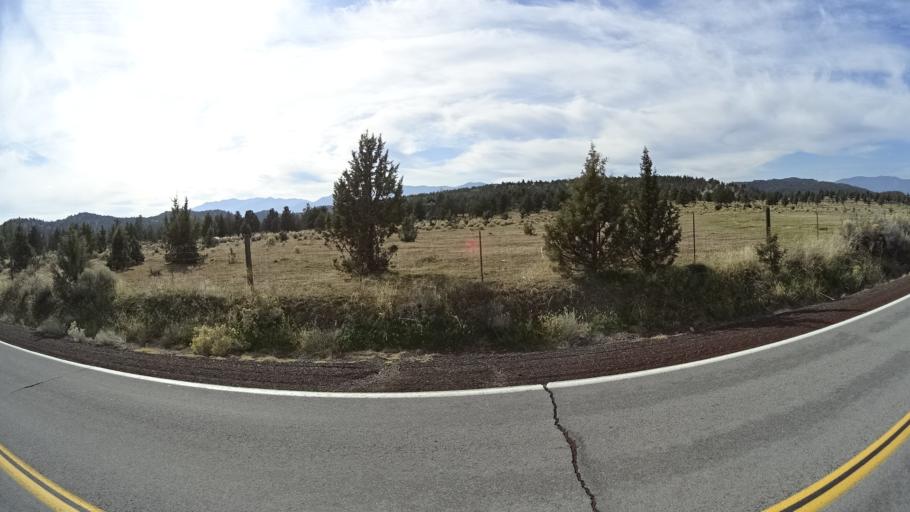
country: US
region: California
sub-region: Siskiyou County
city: Weed
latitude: 41.5531
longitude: -122.3817
